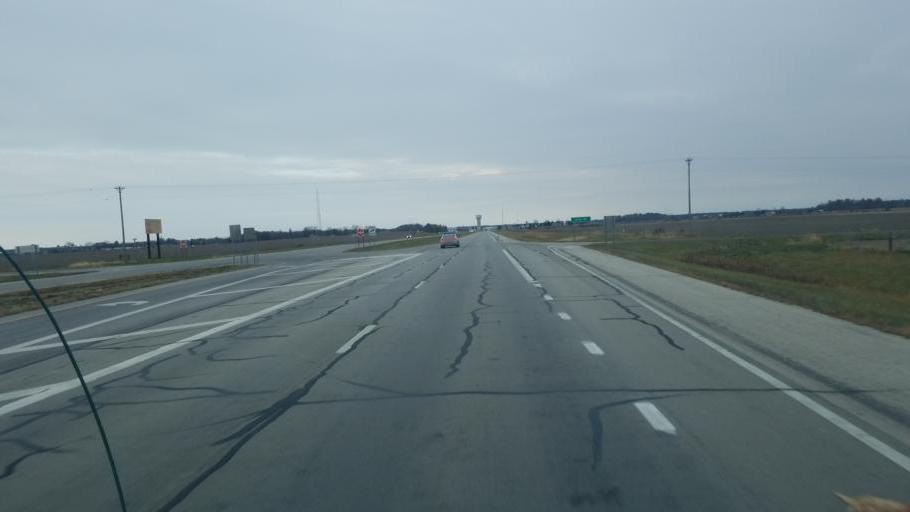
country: US
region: Ohio
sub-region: Mercer County
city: Celina
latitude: 40.5574
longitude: -84.4929
